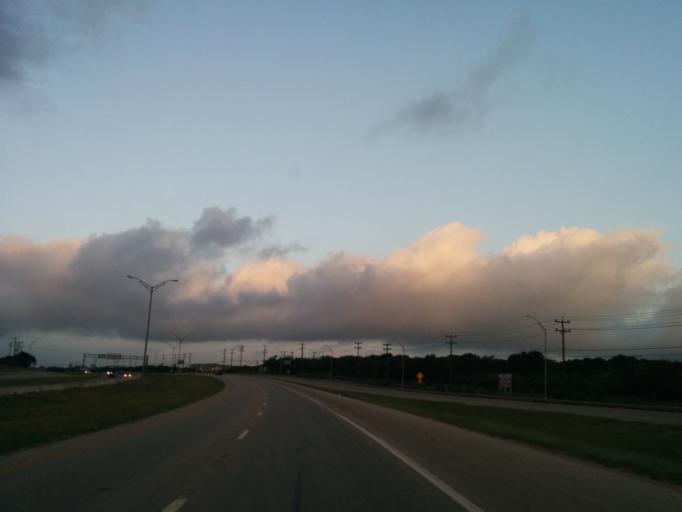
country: US
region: Texas
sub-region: Bexar County
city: Helotes
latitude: 29.5867
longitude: -98.6347
